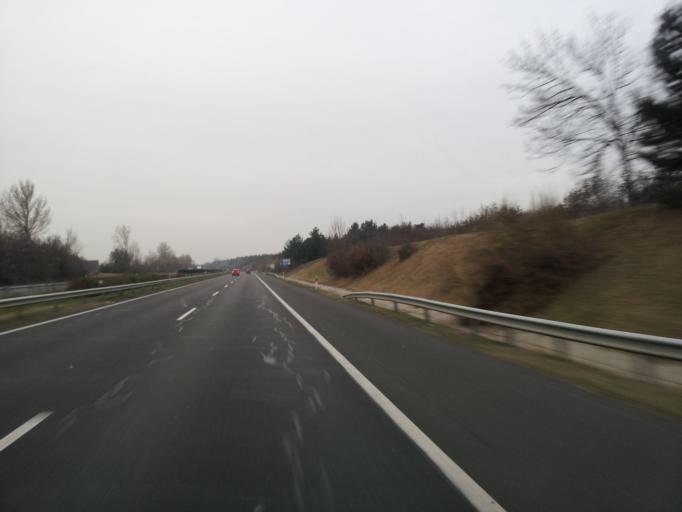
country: HU
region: Fejer
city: Martonvasar
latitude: 47.3194
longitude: 18.7583
